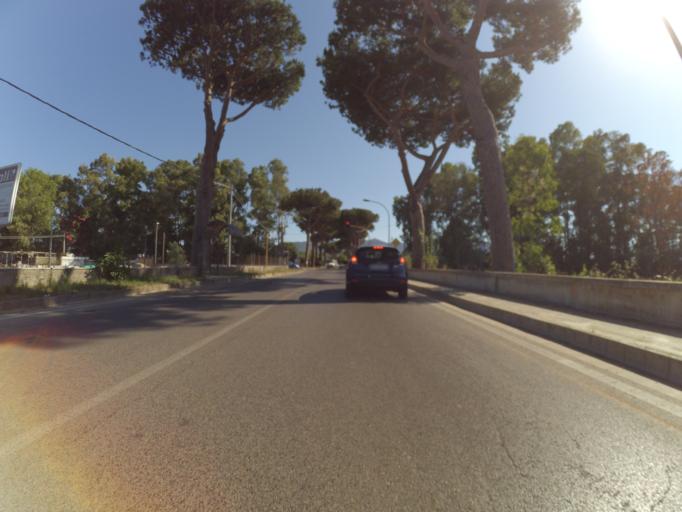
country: IT
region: Latium
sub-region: Provincia di Latina
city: San Felice Circeo
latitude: 41.2654
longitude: 13.0947
